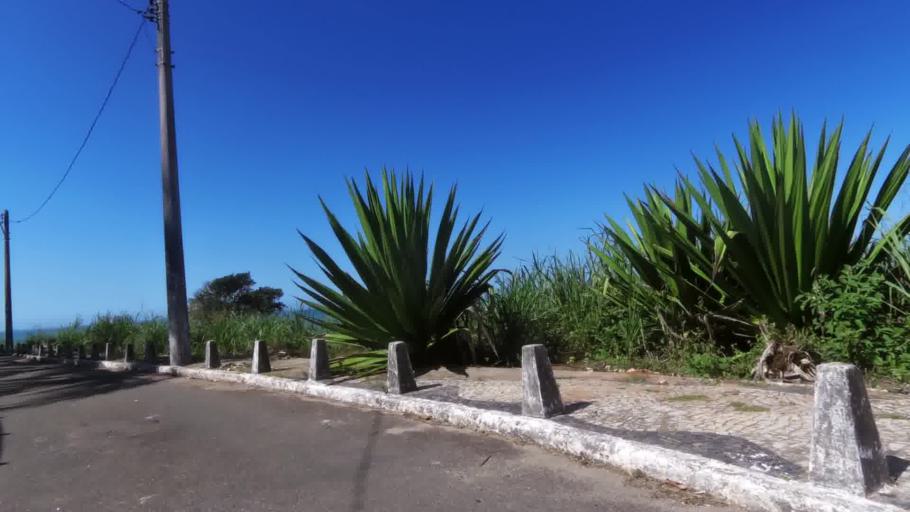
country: BR
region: Espirito Santo
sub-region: Guarapari
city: Guarapari
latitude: -20.7443
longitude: -40.5370
